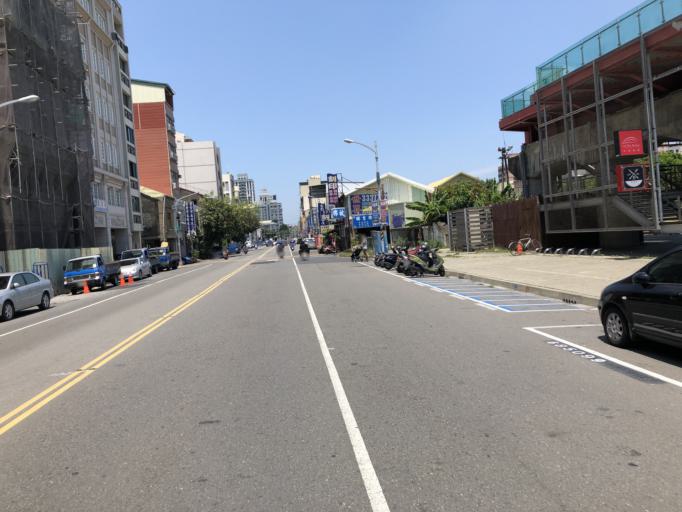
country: TW
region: Kaohsiung
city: Kaohsiung
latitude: 22.6243
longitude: 120.2767
